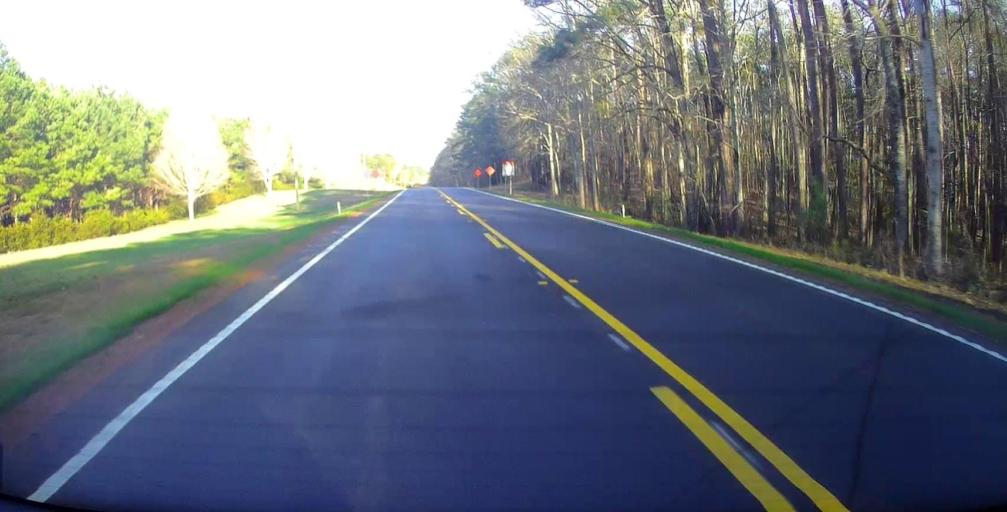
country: US
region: Georgia
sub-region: Harris County
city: Hamilton
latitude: 32.7472
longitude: -85.0080
